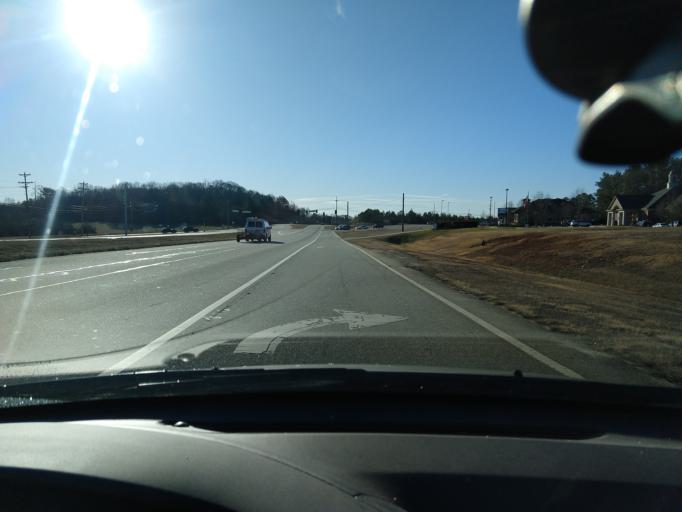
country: US
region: Georgia
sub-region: Jackson County
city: Commerce
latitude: 34.2352
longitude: -83.4534
